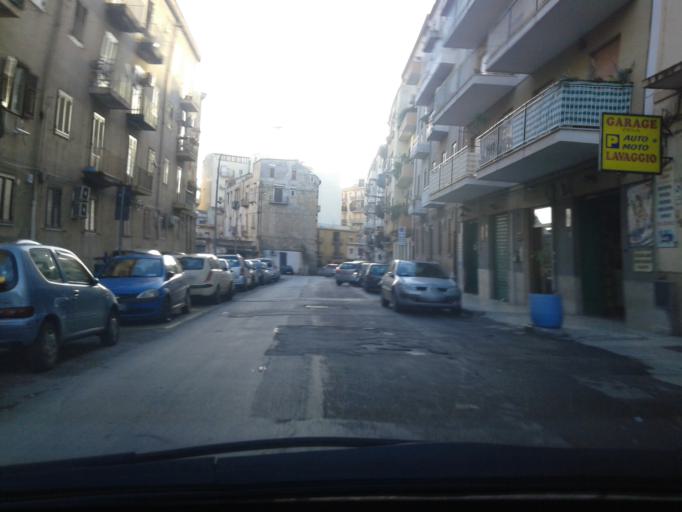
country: IT
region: Sicily
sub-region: Palermo
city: Palermo
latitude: 38.1157
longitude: 13.3444
